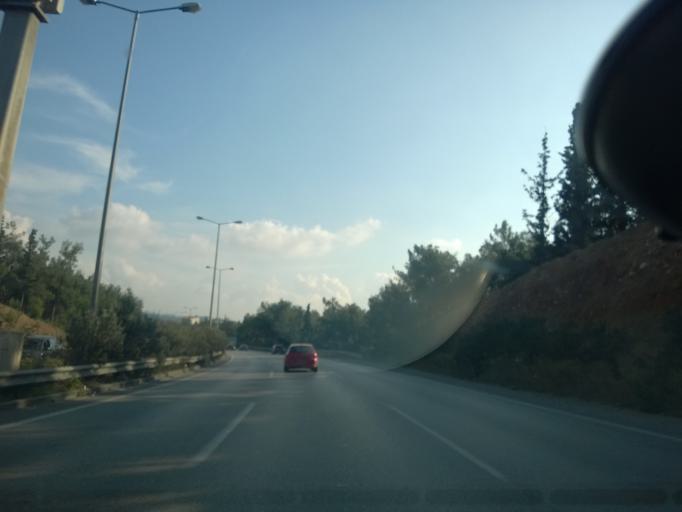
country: GR
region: Central Macedonia
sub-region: Nomos Thessalonikis
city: Triandria
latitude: 40.6172
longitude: 22.9838
